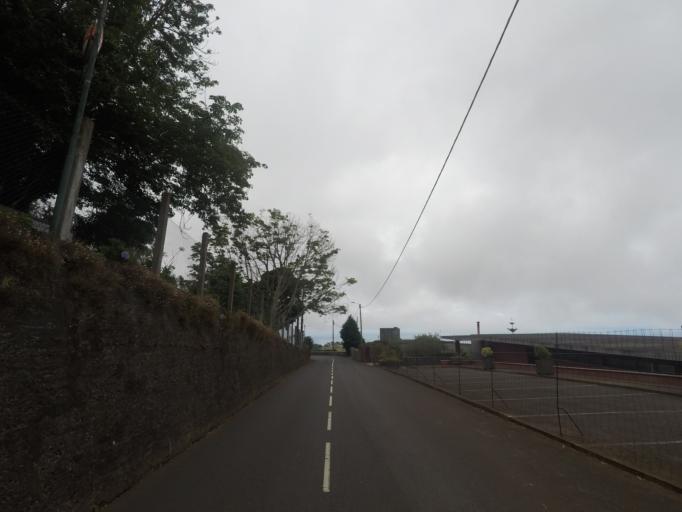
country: PT
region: Madeira
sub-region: Funchal
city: Nossa Senhora do Monte
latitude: 32.6670
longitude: -16.8782
